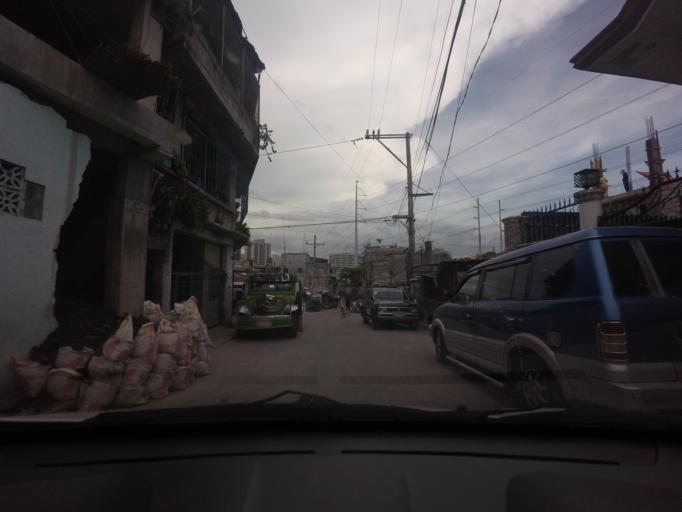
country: PH
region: Calabarzon
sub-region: Province of Rizal
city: Taguig
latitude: 14.5242
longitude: 121.0603
